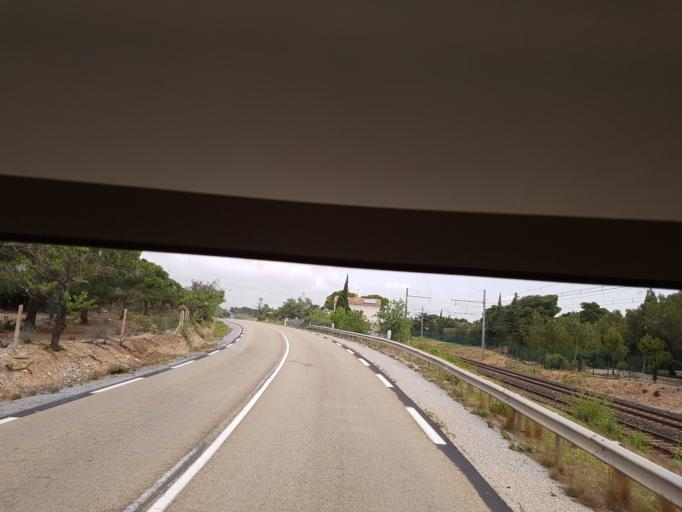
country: FR
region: Languedoc-Roussillon
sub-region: Departement de l'Aude
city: Leucate
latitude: 42.8773
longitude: 2.9932
